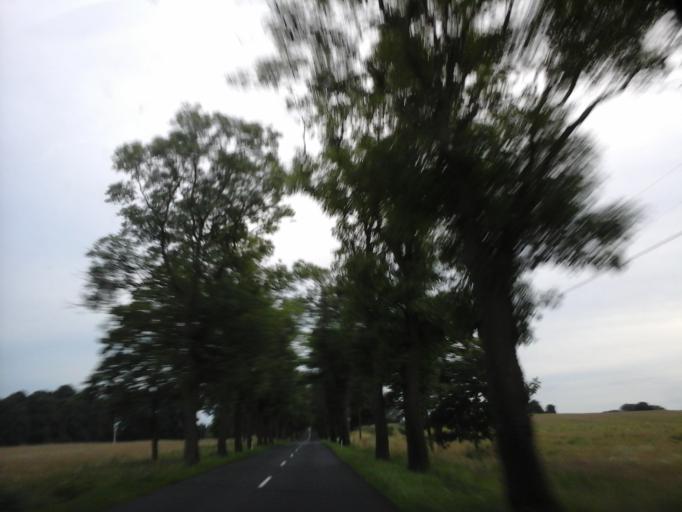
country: PL
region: West Pomeranian Voivodeship
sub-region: Powiat goleniowski
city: Maszewo
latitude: 53.5192
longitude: 15.1022
